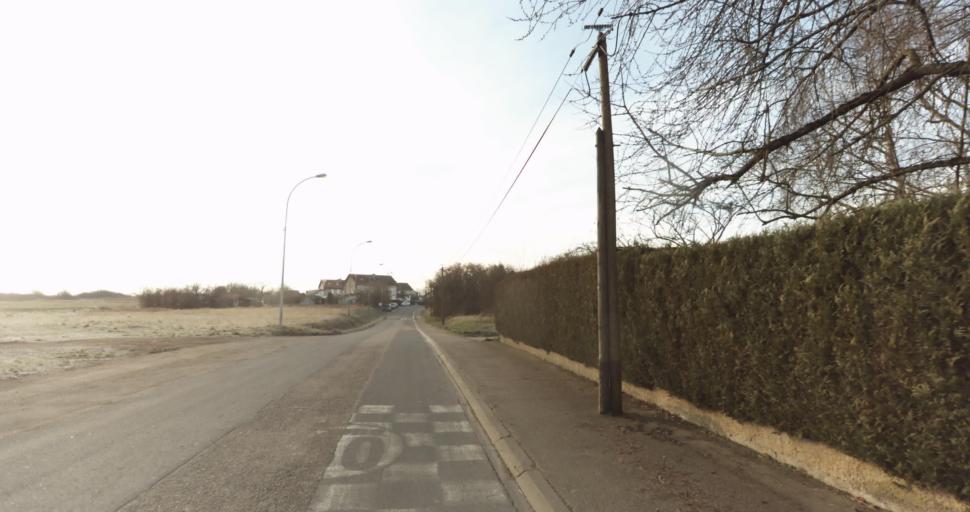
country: FR
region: Lorraine
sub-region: Departement de Meurthe-et-Moselle
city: Labry
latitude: 49.1656
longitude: 5.8881
